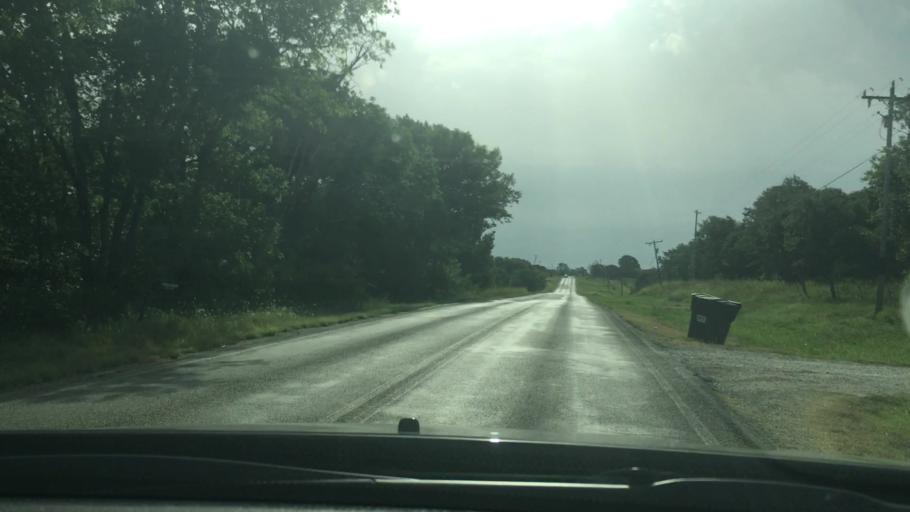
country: US
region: Oklahoma
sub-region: Pontotoc County
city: Byng
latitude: 34.8648
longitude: -96.6113
